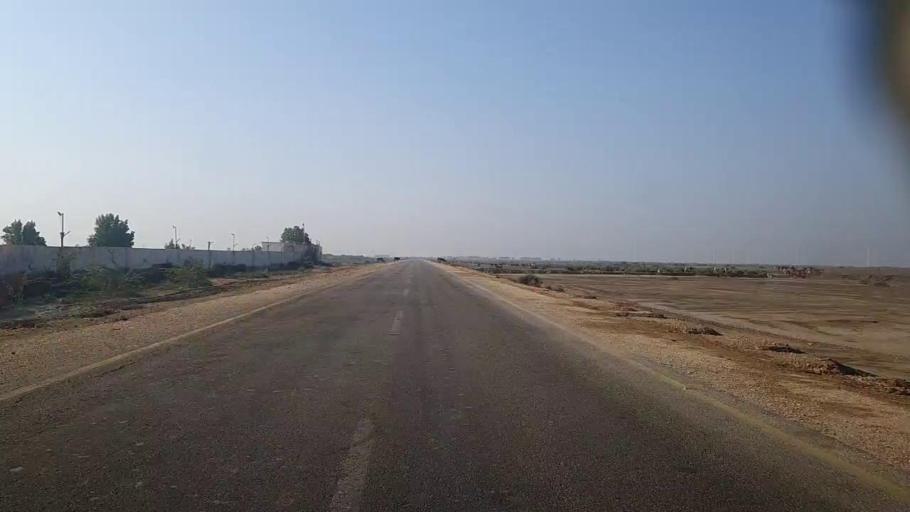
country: PK
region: Sindh
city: Gharo
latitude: 24.6996
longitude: 67.5271
